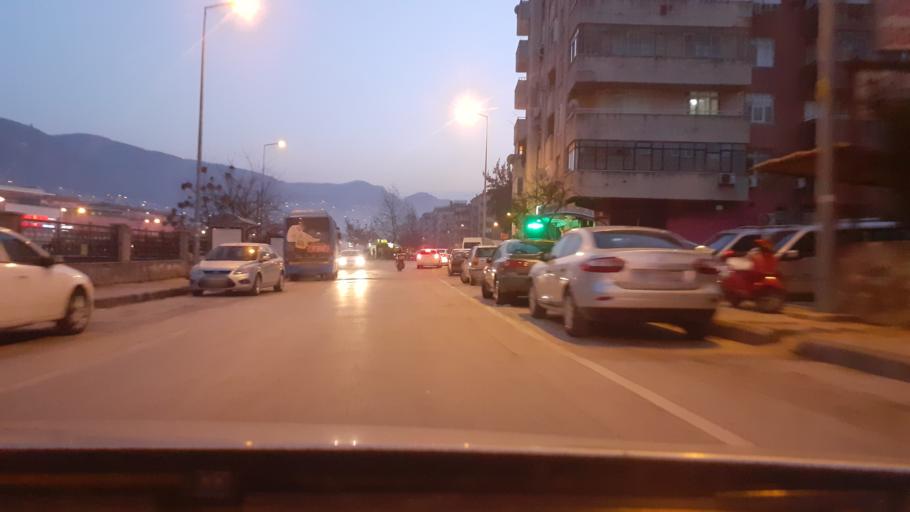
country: TR
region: Hatay
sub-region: Antakya Ilcesi
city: Antakya
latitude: 36.2109
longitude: 36.1615
